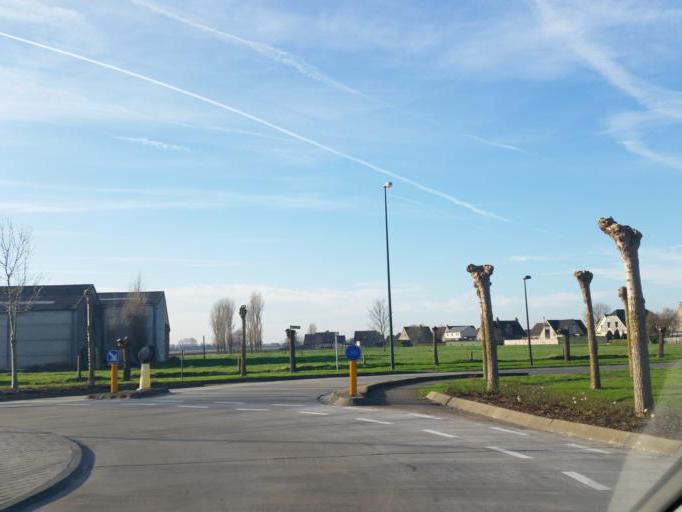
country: BE
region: Flanders
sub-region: Provincie West-Vlaanderen
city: De Haan
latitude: 51.2590
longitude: 3.0291
